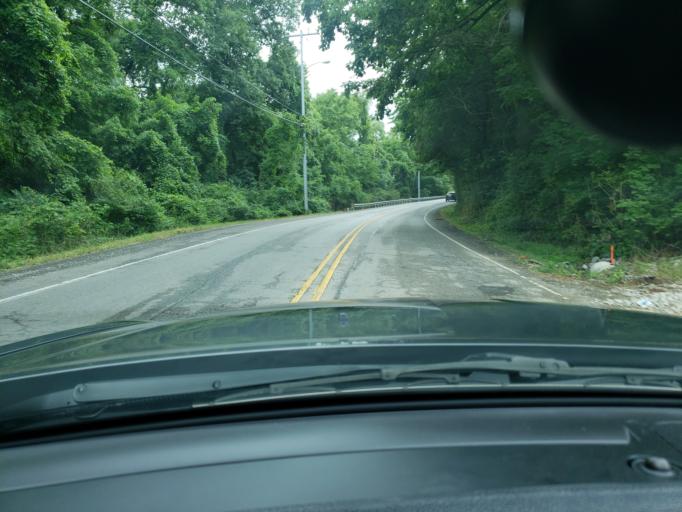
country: US
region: Tennessee
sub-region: Williamson County
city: Nolensville
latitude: 36.0443
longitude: -86.6750
